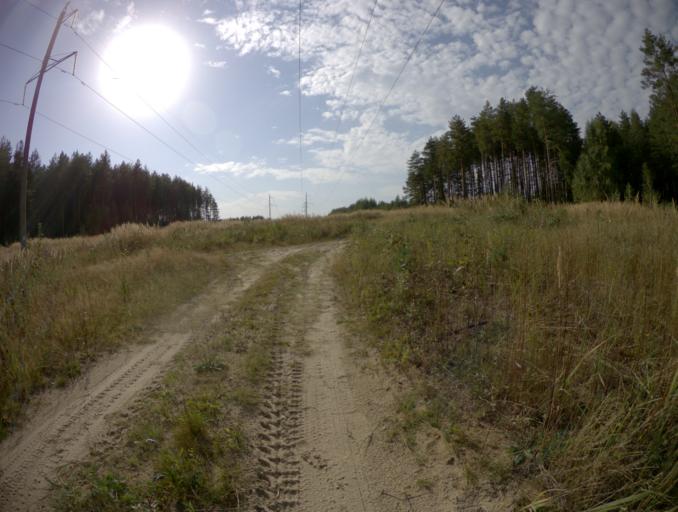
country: RU
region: Vladimir
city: Raduzhnyy
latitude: 56.0152
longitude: 40.2962
